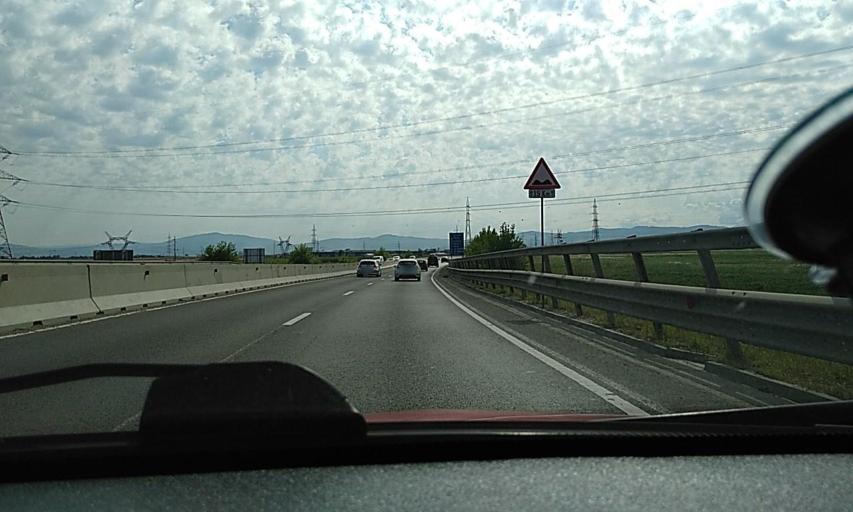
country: RO
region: Brasov
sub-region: Comuna Sanpetru
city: Sanpetru
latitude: 45.6839
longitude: 25.6486
